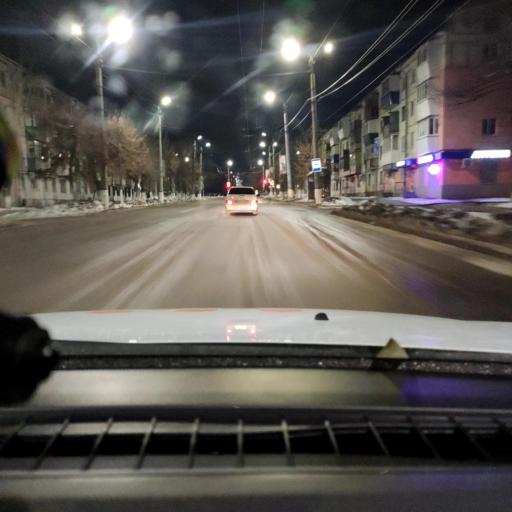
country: RU
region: Samara
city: Novokuybyshevsk
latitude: 53.0877
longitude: 49.9505
